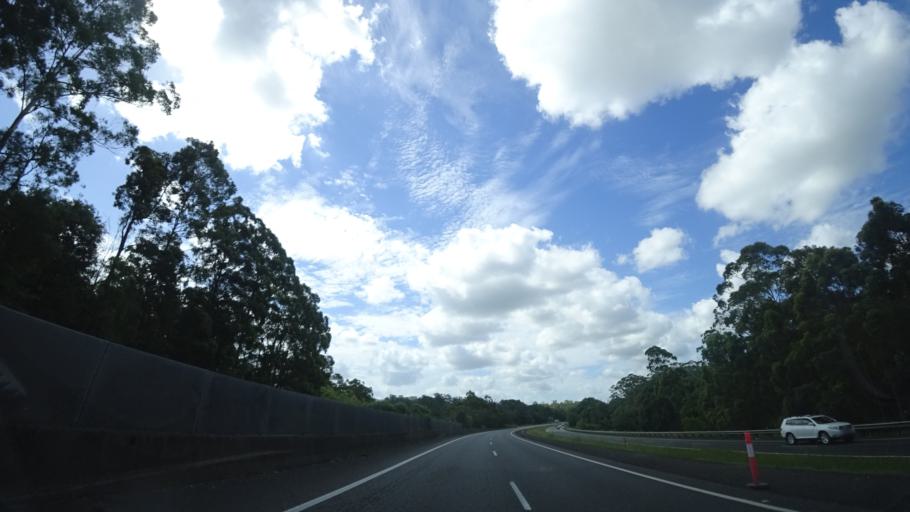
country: AU
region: Queensland
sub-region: Sunshine Coast
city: Yandina
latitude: -26.5833
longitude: 152.9650
